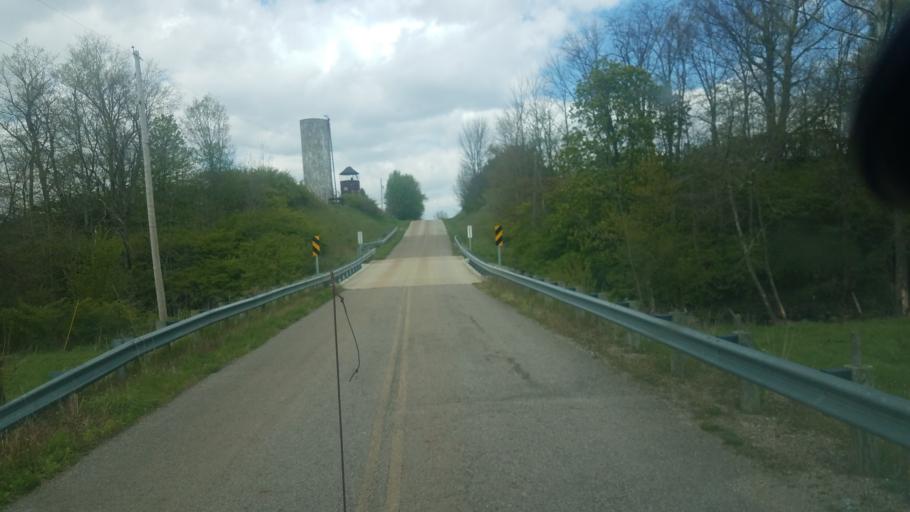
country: US
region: Ohio
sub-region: Crawford County
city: Galion
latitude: 40.7231
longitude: -82.8347
